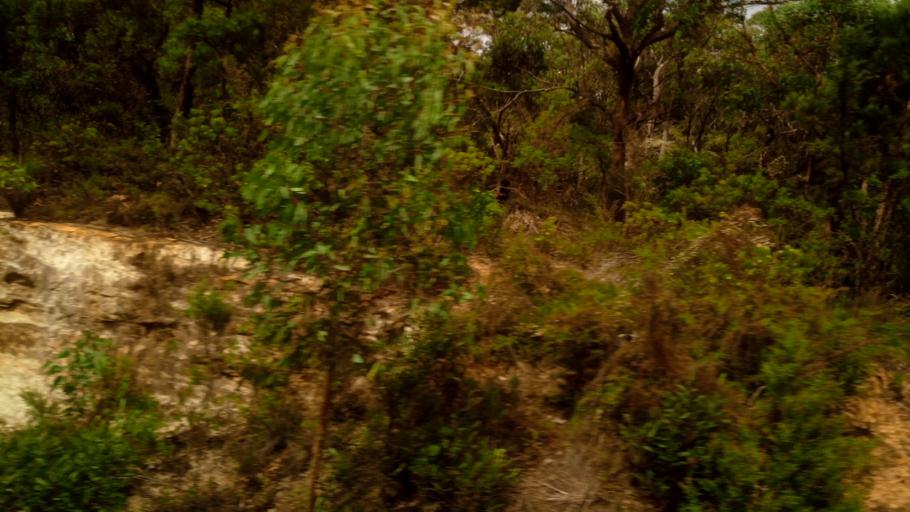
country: AU
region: New South Wales
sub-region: Blue Mountains Municipality
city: Lawson
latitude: -33.7176
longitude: 150.3854
